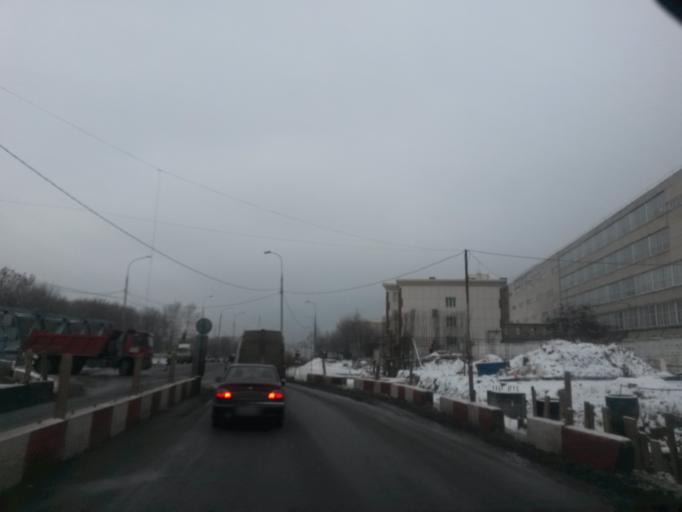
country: RU
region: Moscow
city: Mikhalkovo
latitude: 55.6792
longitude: 37.4340
